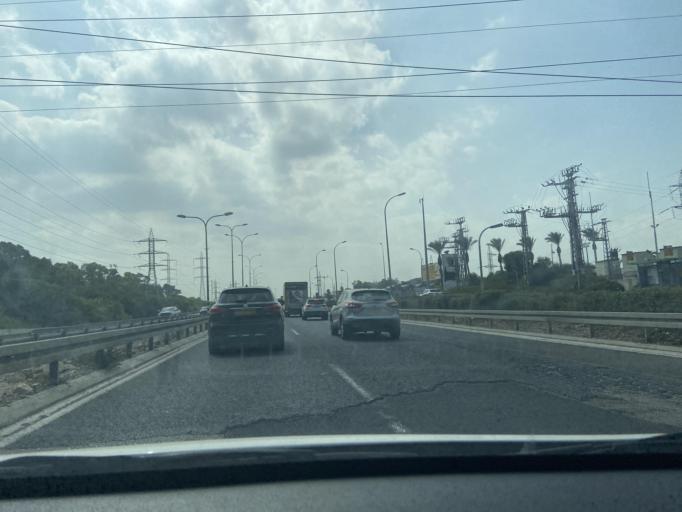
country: IL
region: Northern District
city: `Akko
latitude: 32.8948
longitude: 35.0937
